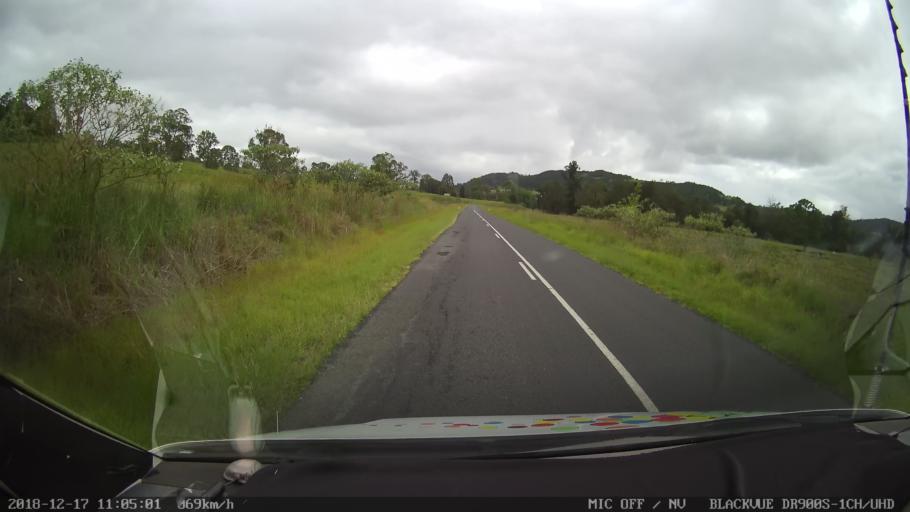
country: AU
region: New South Wales
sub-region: Kyogle
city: Kyogle
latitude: -28.7931
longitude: 152.6445
